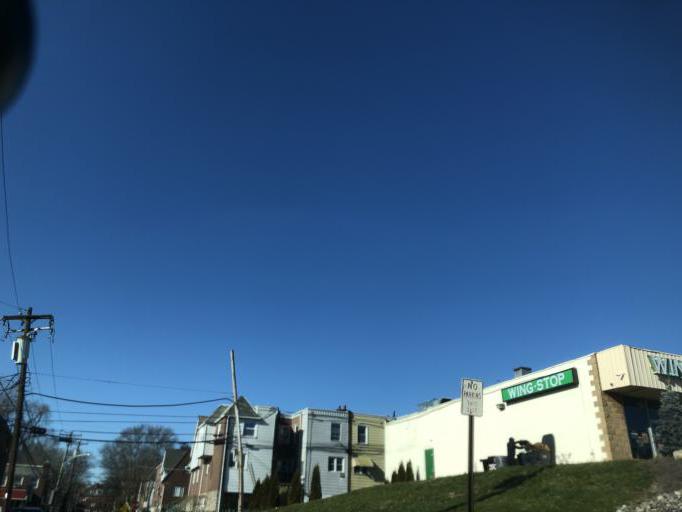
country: US
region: Pennsylvania
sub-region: Delaware County
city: East Lansdowne
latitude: 39.9551
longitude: -75.2584
